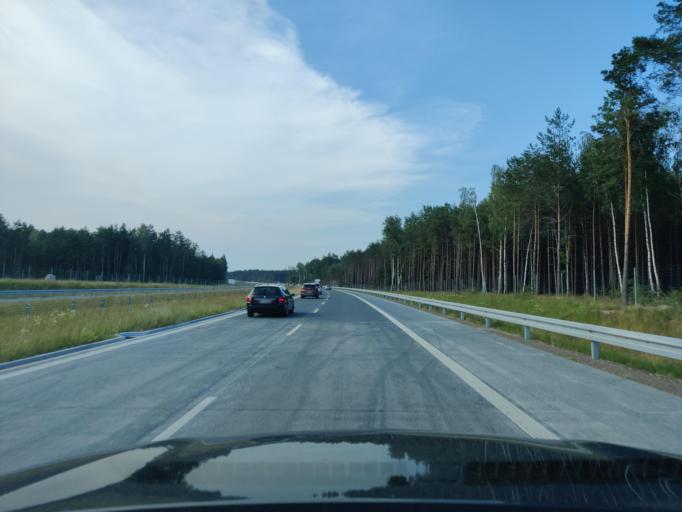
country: PL
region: Masovian Voivodeship
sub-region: Powiat mlawski
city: Strzegowo
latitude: 52.9143
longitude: 20.2838
